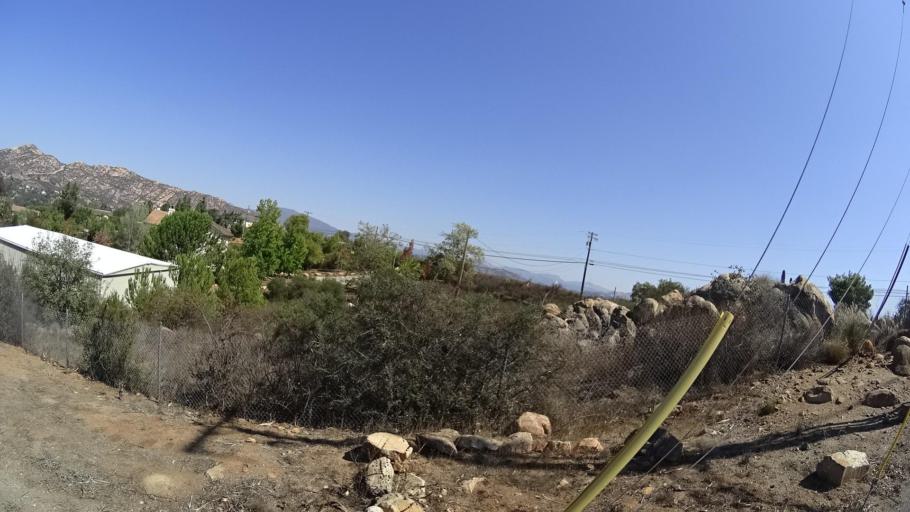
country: US
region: California
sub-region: San Diego County
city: Crest
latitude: 32.8201
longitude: -116.8542
